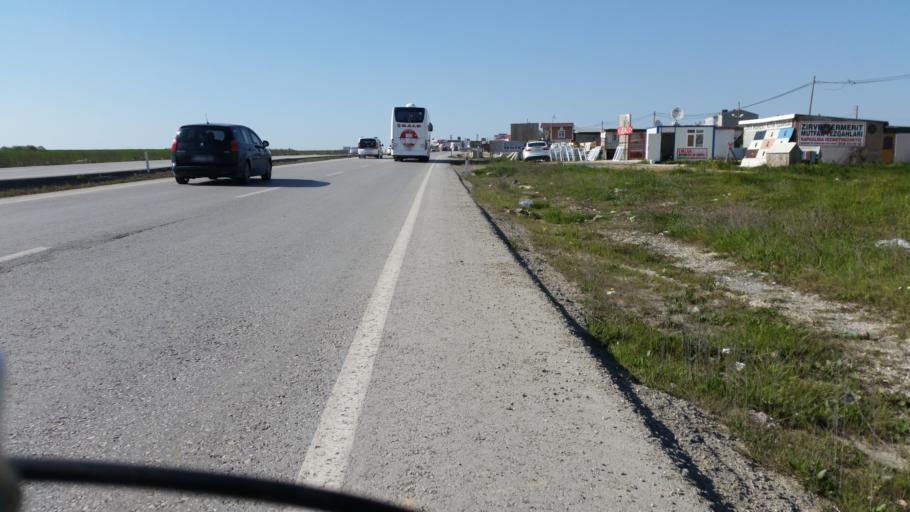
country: TR
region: Tekirdag
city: Cerkezkoey
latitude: 41.3376
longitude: 27.9671
